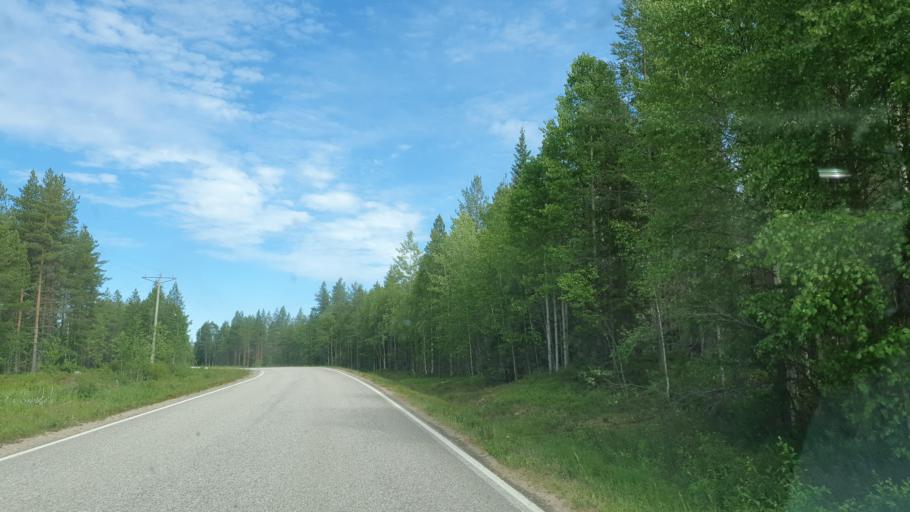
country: FI
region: Kainuu
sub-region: Kehys-Kainuu
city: Suomussalmi
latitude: 64.5655
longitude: 28.9744
